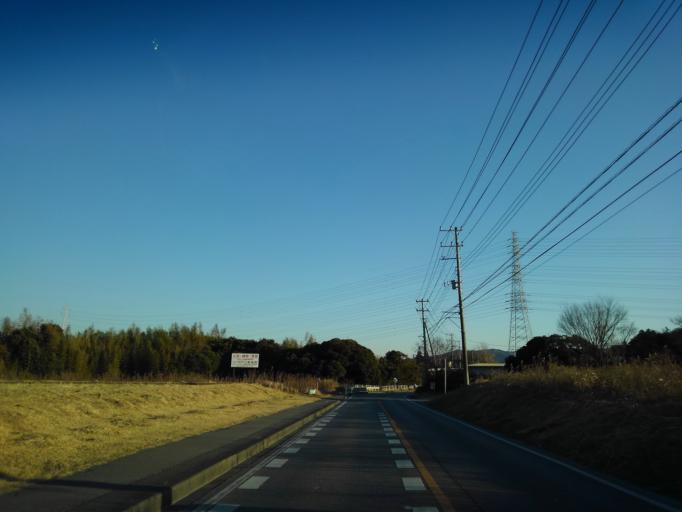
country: JP
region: Chiba
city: Kimitsu
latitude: 35.3126
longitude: 139.9358
